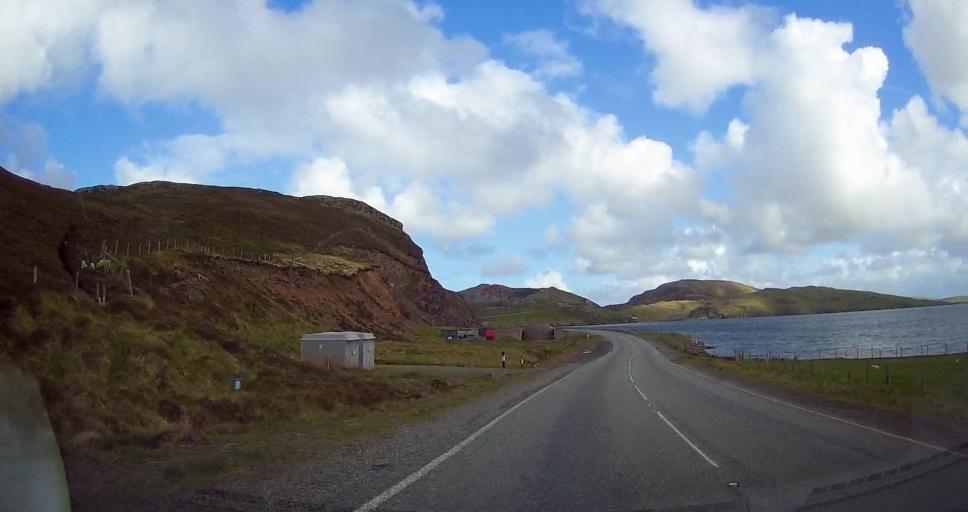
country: GB
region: Scotland
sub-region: Shetland Islands
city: Lerwick
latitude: 60.3931
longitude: -1.3779
